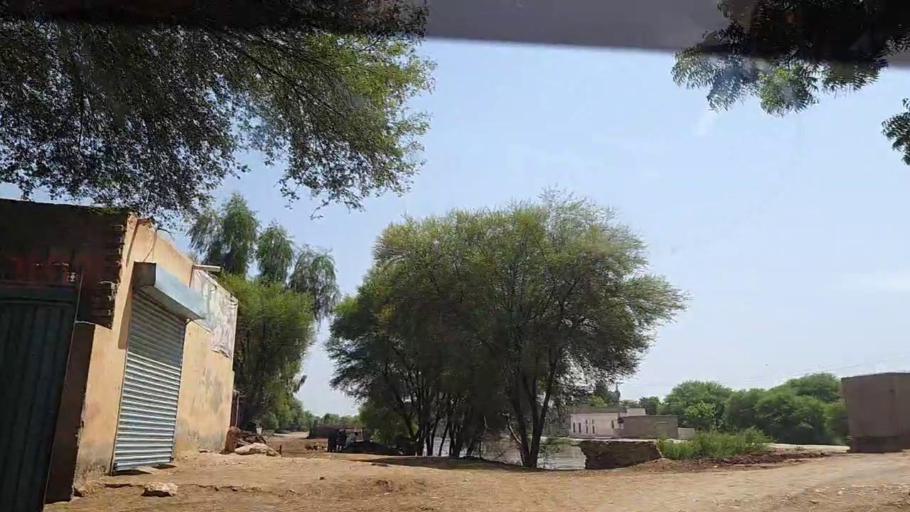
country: PK
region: Sindh
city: Ghauspur
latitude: 28.1670
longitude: 69.1264
